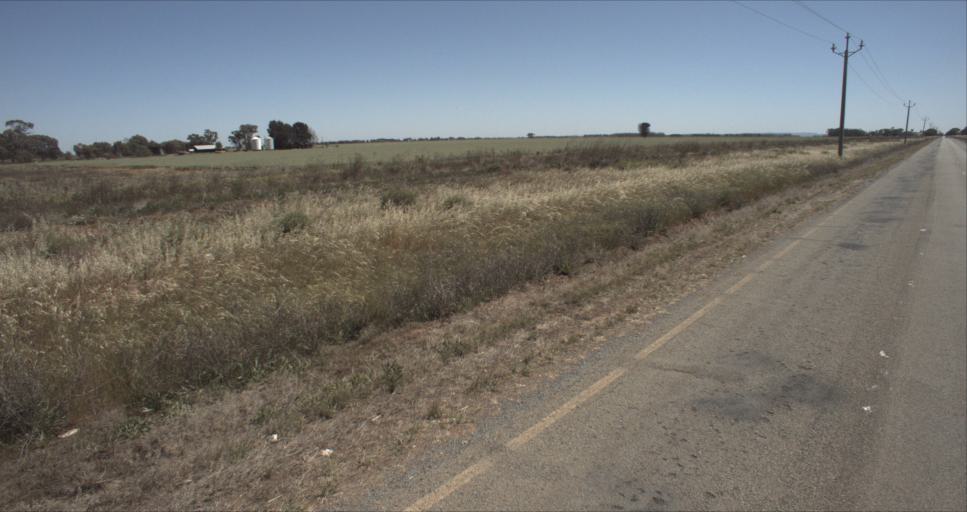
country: AU
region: New South Wales
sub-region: Leeton
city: Leeton
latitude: -34.5131
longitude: 146.2847
